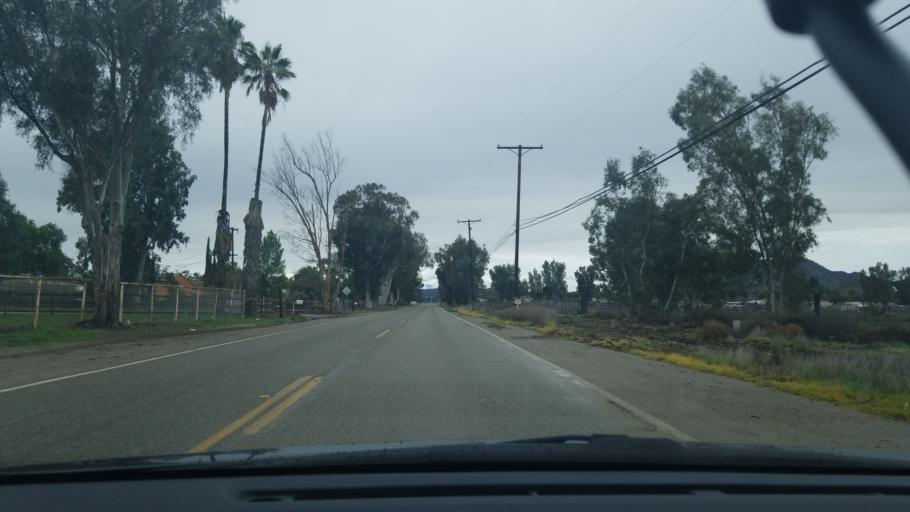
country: US
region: California
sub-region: Riverside County
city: Winchester
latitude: 33.7072
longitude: -117.0766
